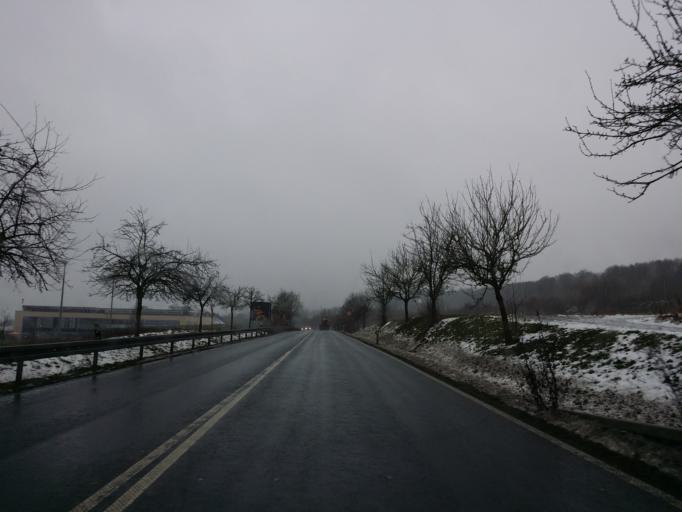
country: DE
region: Hesse
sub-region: Regierungsbezirk Darmstadt
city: Idstein
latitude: 50.2232
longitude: 8.2539
